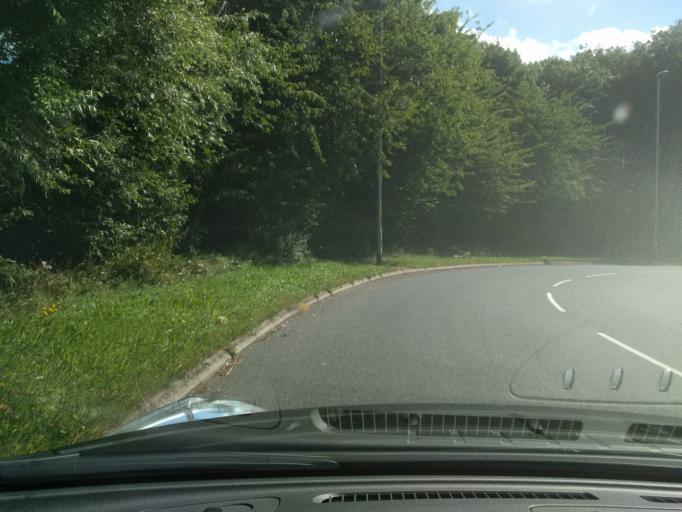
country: GB
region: England
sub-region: Warrington
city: Croft
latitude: 53.4068
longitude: -2.5235
